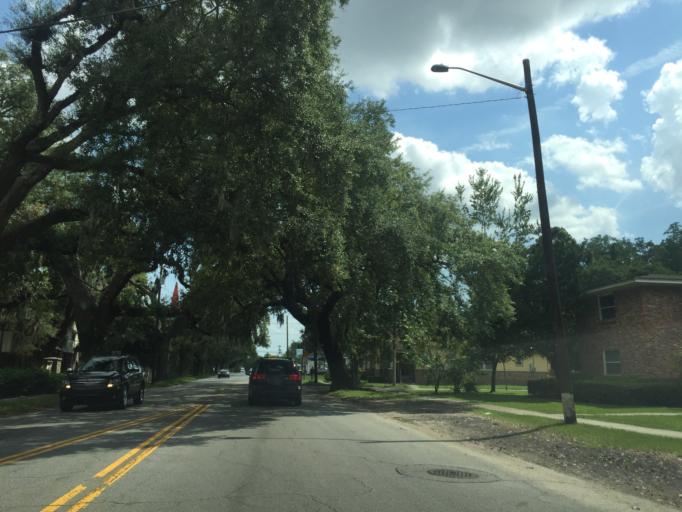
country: US
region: Georgia
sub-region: Chatham County
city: Savannah
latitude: 32.0457
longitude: -81.1047
